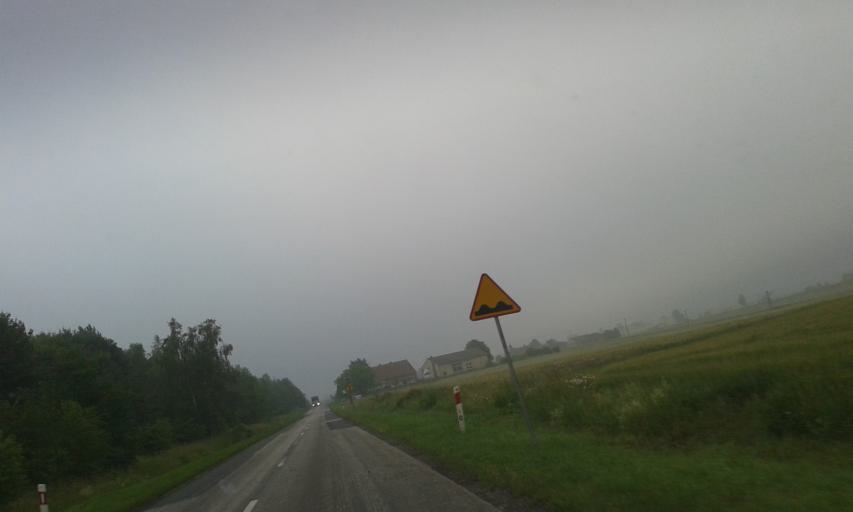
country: PL
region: Pomeranian Voivodeship
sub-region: Powiat czluchowski
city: Debrzno
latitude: 53.5179
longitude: 17.2345
